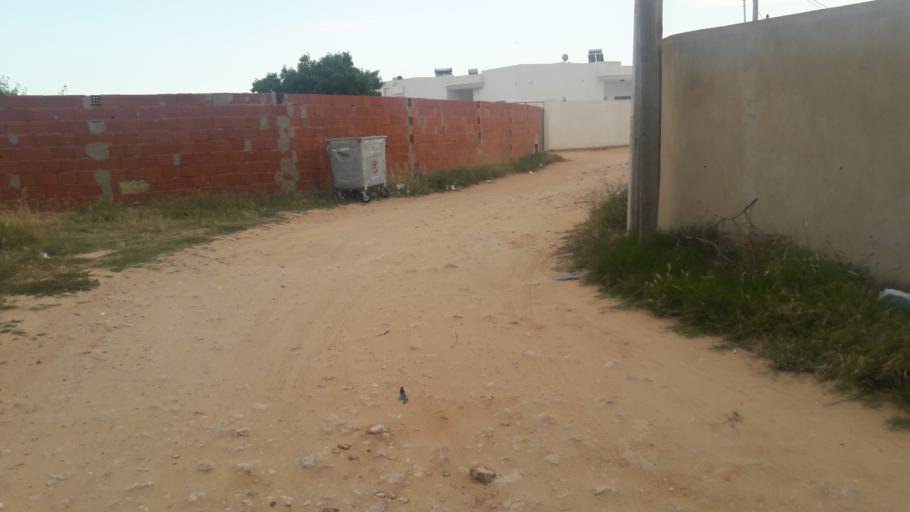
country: TN
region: Safaqis
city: Al Qarmadah
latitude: 34.8122
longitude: 10.7467
